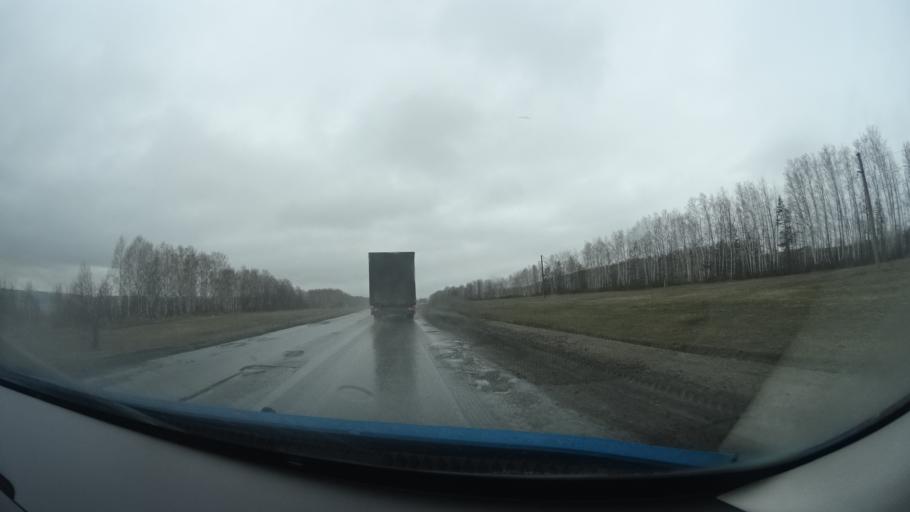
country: RU
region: Bashkortostan
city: Kandry
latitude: 54.5173
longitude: 54.0464
